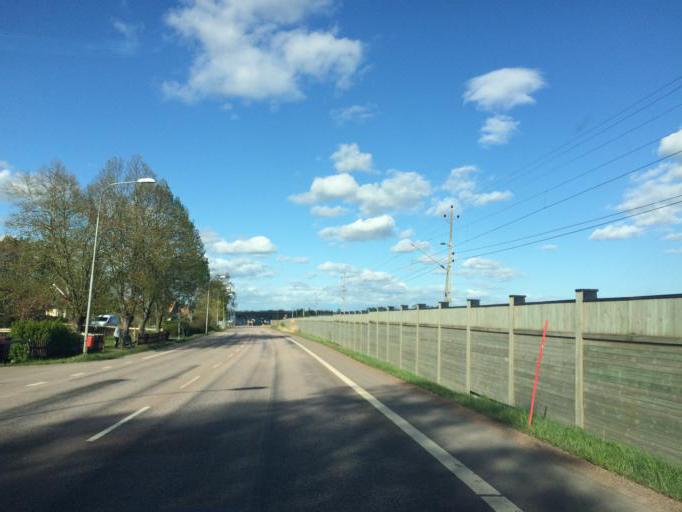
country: SE
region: Vaestmanland
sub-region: Hallstahammars Kommun
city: Kolback
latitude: 59.5576
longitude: 16.2170
